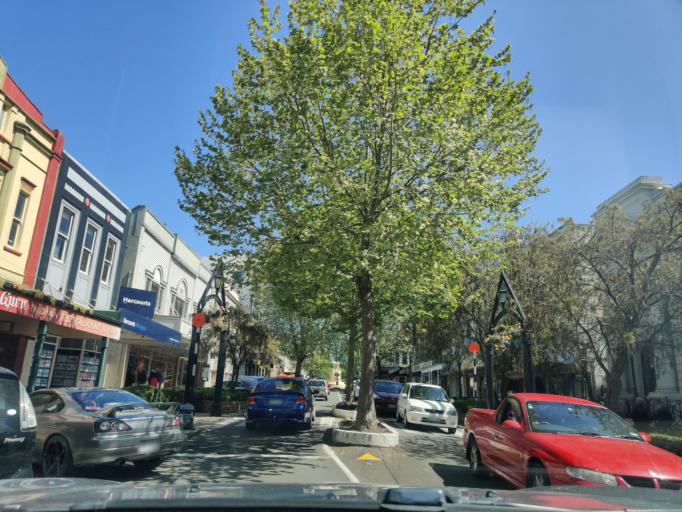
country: NZ
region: Manawatu-Wanganui
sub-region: Wanganui District
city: Wanganui
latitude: -39.9346
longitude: 175.0548
